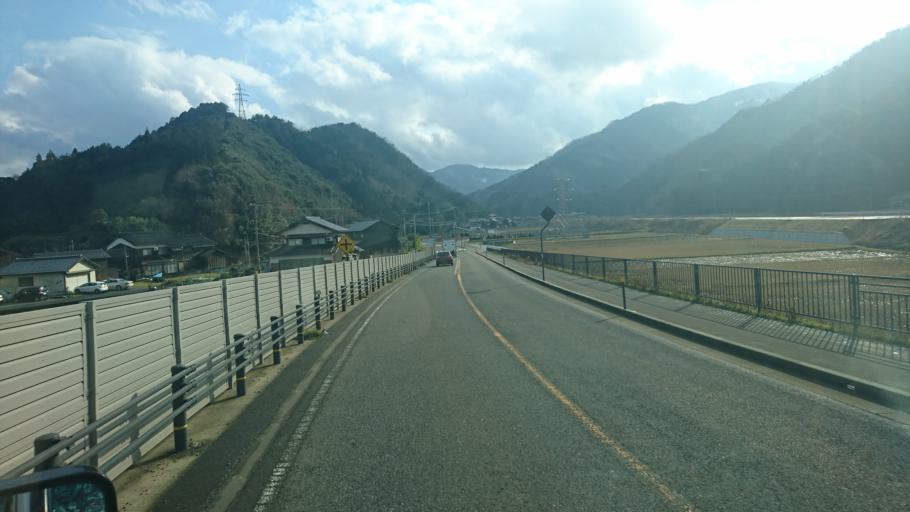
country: JP
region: Tottori
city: Tottori
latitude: 35.6079
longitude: 134.4704
